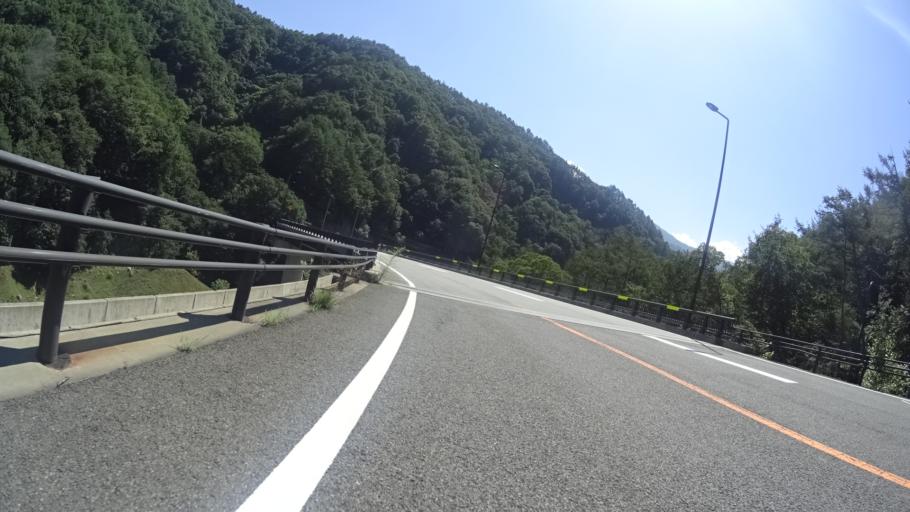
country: JP
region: Yamanashi
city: Enzan
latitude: 35.7634
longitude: 138.8046
